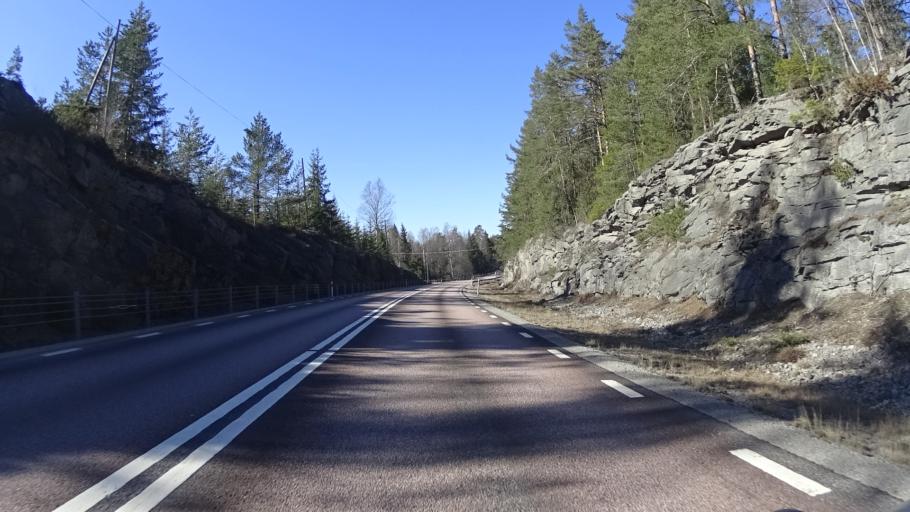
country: SE
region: Vaermland
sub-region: Karlstads Kommun
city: Edsvalla
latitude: 59.6067
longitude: 12.9923
